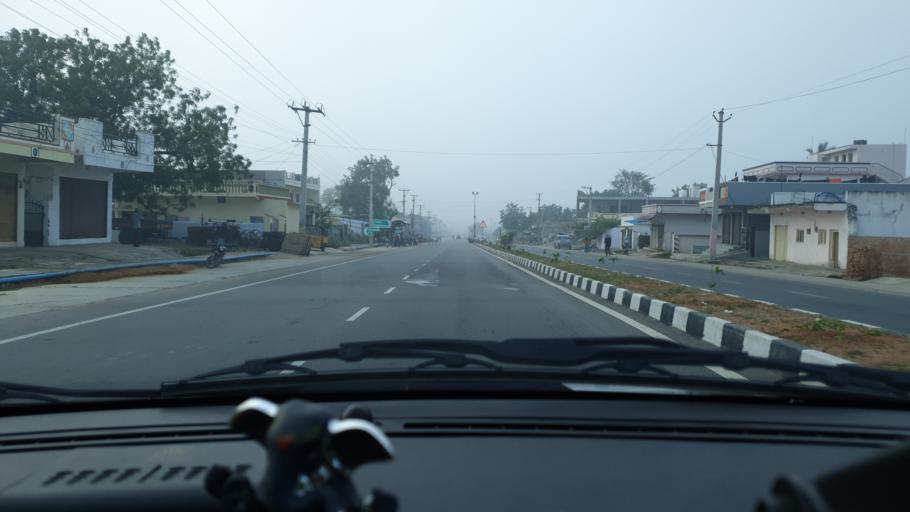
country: IN
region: Telangana
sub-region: Mahbubnagar
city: Farrukhnagar
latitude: 16.8819
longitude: 78.5291
